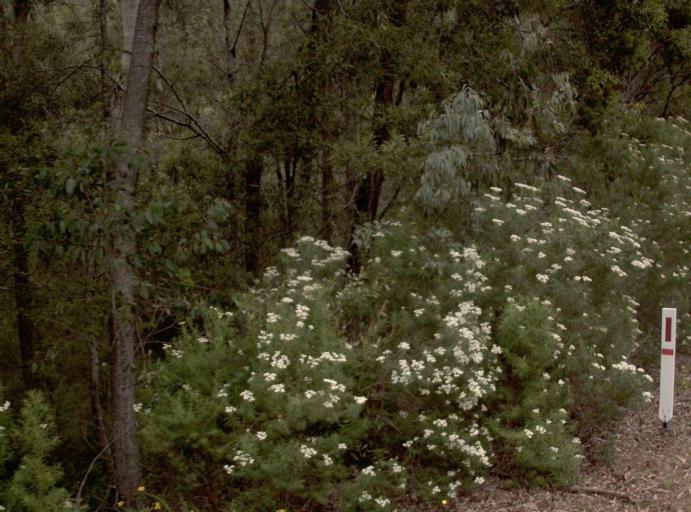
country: AU
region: Victoria
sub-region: East Gippsland
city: Bairnsdale
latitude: -37.6406
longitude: 147.2634
